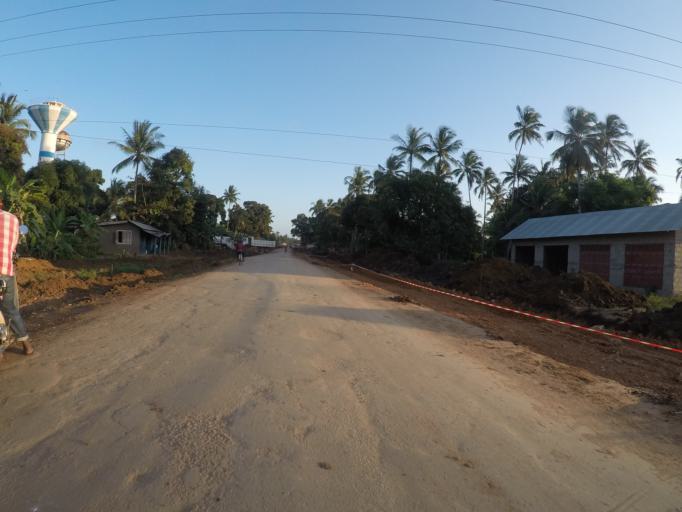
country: TZ
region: Zanzibar North
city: Gamba
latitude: -5.9228
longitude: 39.2999
